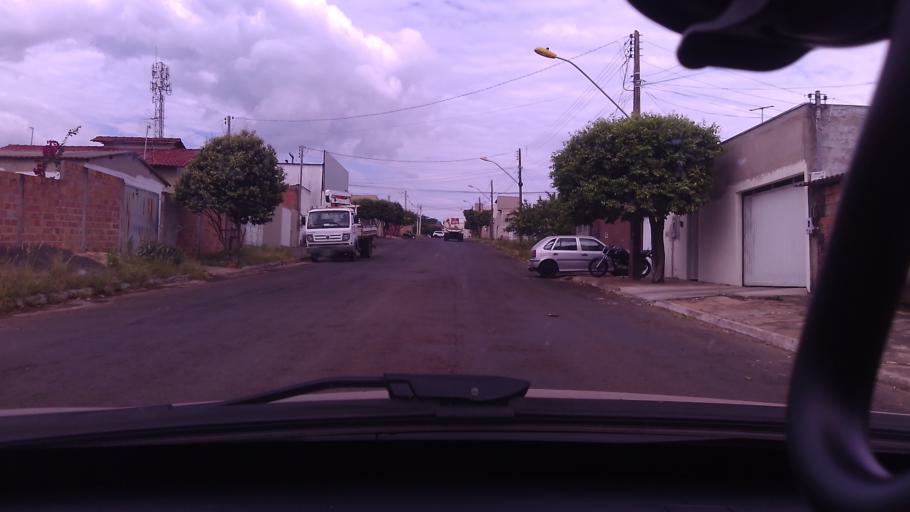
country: BR
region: Goias
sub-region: Mineiros
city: Mineiros
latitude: -17.5694
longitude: -52.5394
